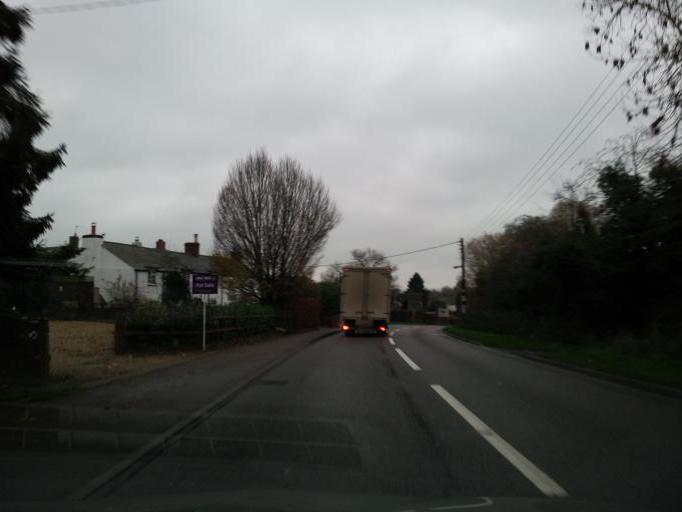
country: GB
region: England
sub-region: Northamptonshire
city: Daventry
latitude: 52.3313
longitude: -1.1762
